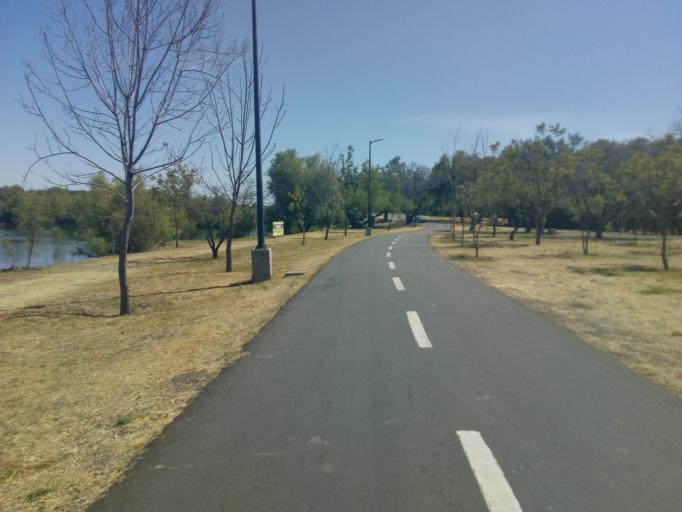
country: MX
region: Guanajuato
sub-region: Leon
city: La Ermita
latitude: 21.1817
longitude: -101.6960
